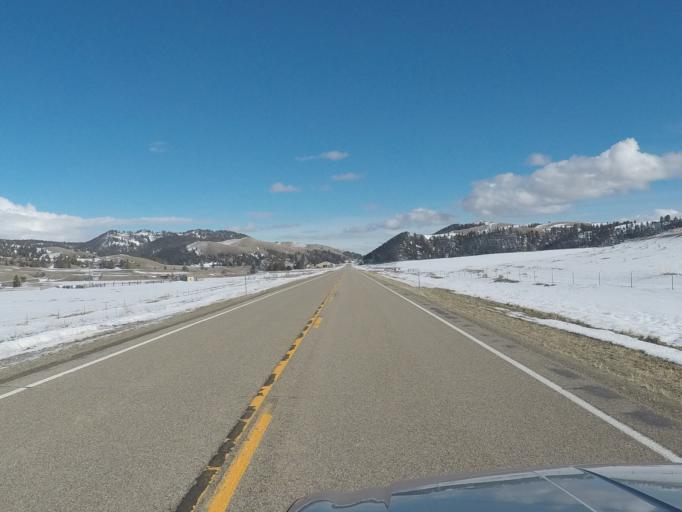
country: US
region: Montana
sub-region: Meagher County
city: White Sulphur Springs
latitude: 46.5704
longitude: -110.5391
